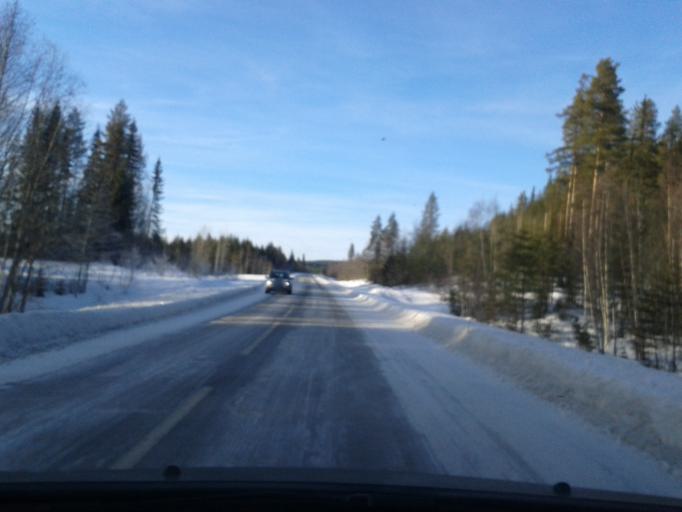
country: SE
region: Vaesternorrland
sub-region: OErnskoeldsviks Kommun
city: Bredbyn
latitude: 63.7490
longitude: 17.7213
